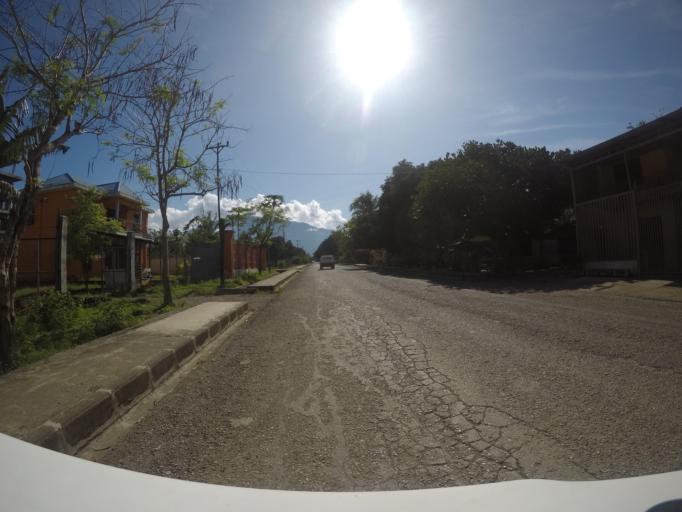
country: TL
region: Bobonaro
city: Maliana
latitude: -8.9914
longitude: 125.1954
